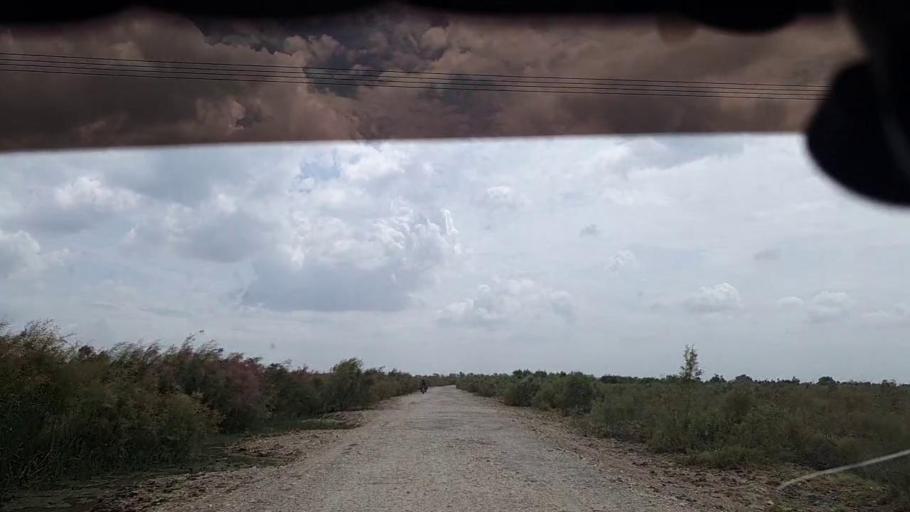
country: PK
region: Sindh
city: Ghauspur
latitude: 28.0650
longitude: 68.9393
